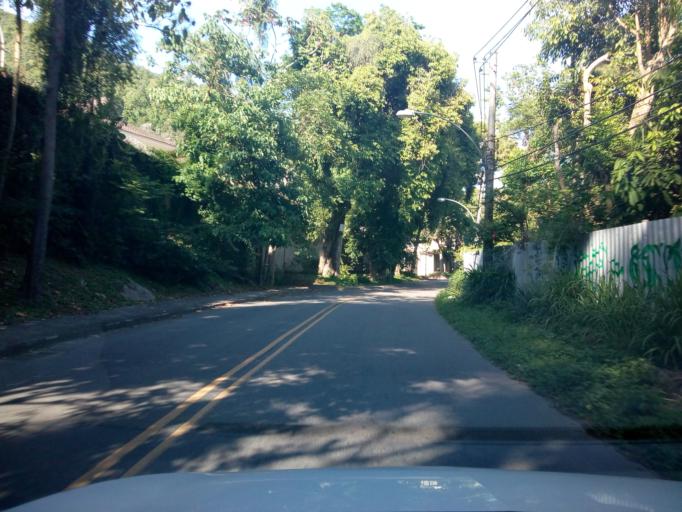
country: BR
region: Rio de Janeiro
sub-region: Nilopolis
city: Nilopolis
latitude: -23.0254
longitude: -43.5036
